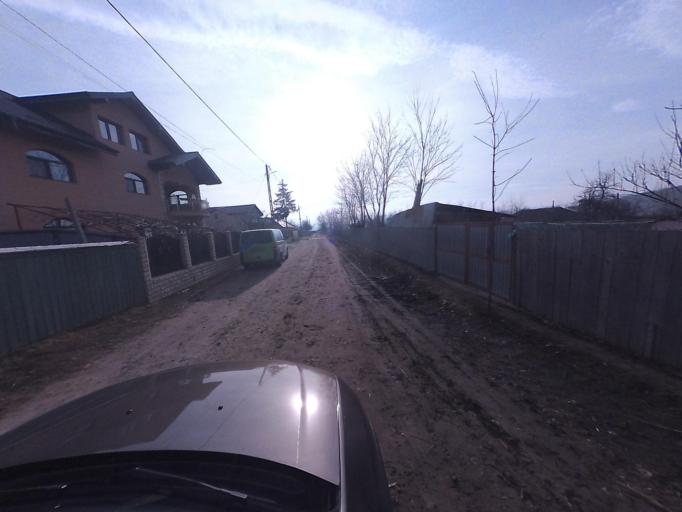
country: RO
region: Vaslui
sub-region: Comuna Solesti
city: Solesti
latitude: 46.8067
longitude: 27.7844
